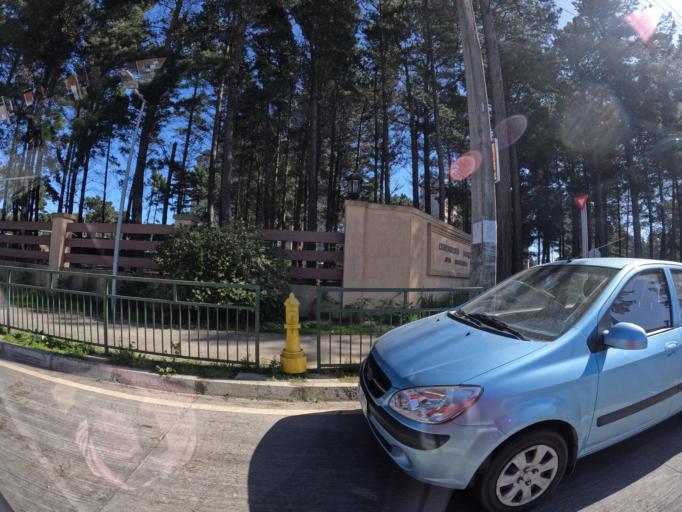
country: CL
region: Biobio
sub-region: Provincia de Concepcion
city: Concepcion
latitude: -36.8856
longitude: -73.1496
